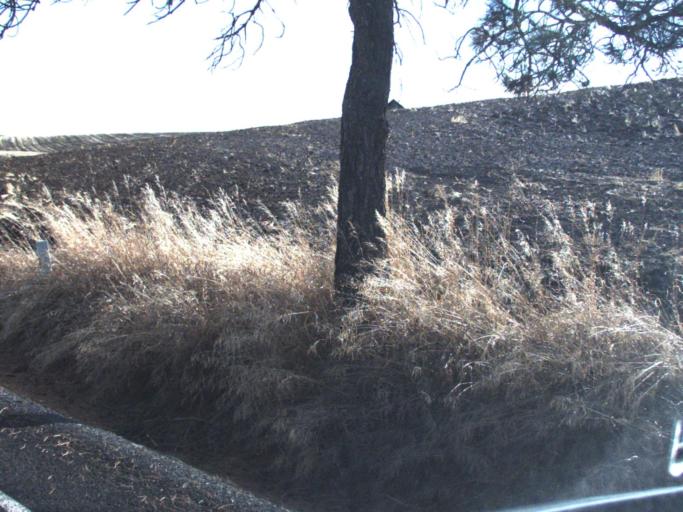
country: US
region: Washington
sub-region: Whitman County
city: Pullman
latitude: 46.9291
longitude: -117.1138
